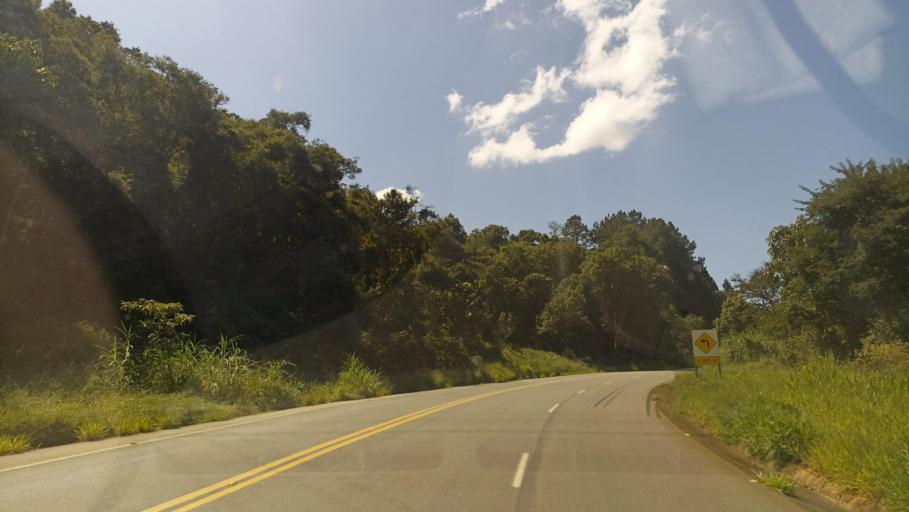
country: BR
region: Sao Paulo
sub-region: Cunha
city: Cunha
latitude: -22.9803
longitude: -45.0436
